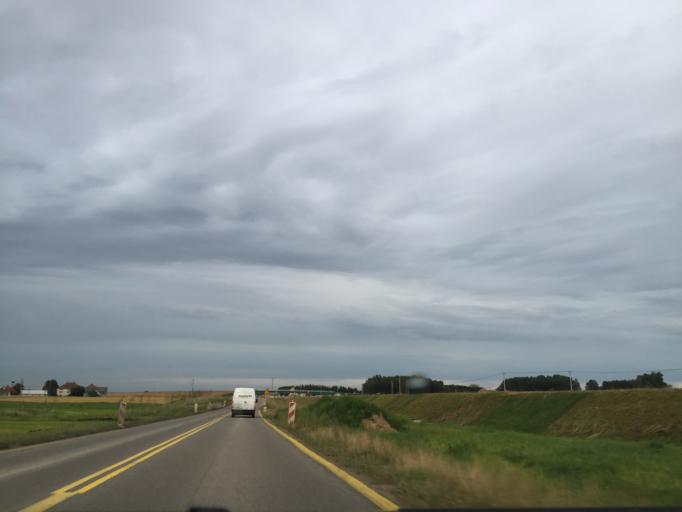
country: PL
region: Podlasie
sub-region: Powiat zambrowski
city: Rutki-Kossaki
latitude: 53.1083
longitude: 22.5745
